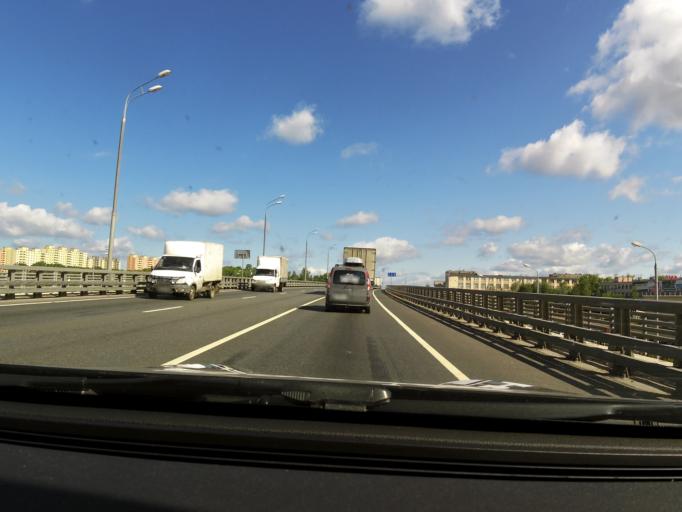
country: RU
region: Tverskaya
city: Tver
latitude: 56.8409
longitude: 35.7932
